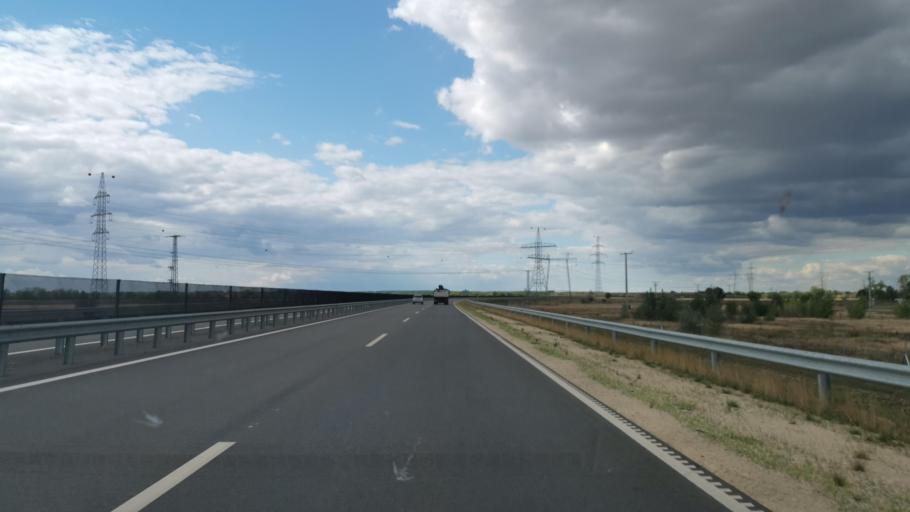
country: HU
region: Jasz-Nagykun-Szolnok
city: Tiszapuspoki
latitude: 47.1875
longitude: 20.3466
